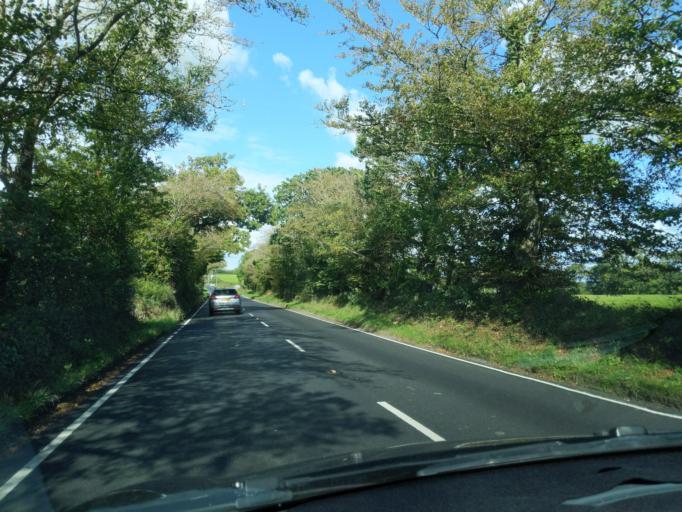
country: GB
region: England
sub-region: Devon
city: Holsworthy
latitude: 50.8202
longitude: -4.3458
